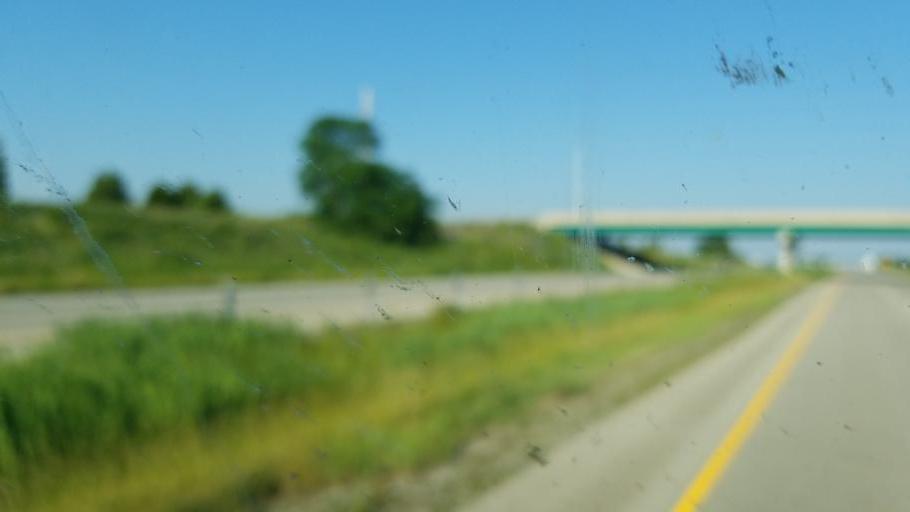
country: US
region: Illinois
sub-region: LaSalle County
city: Marseilles
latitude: 41.3755
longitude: -88.7049
